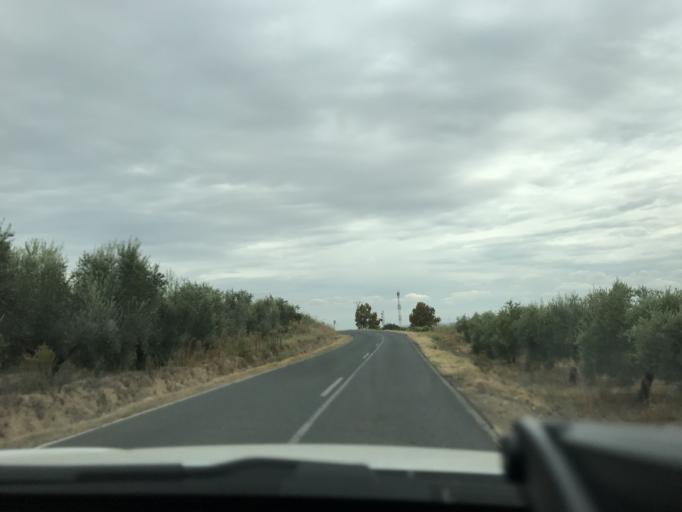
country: ES
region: Andalusia
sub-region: Provincia de Sevilla
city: Villanueva del Rio y Minas
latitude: 37.6424
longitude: -5.7061
